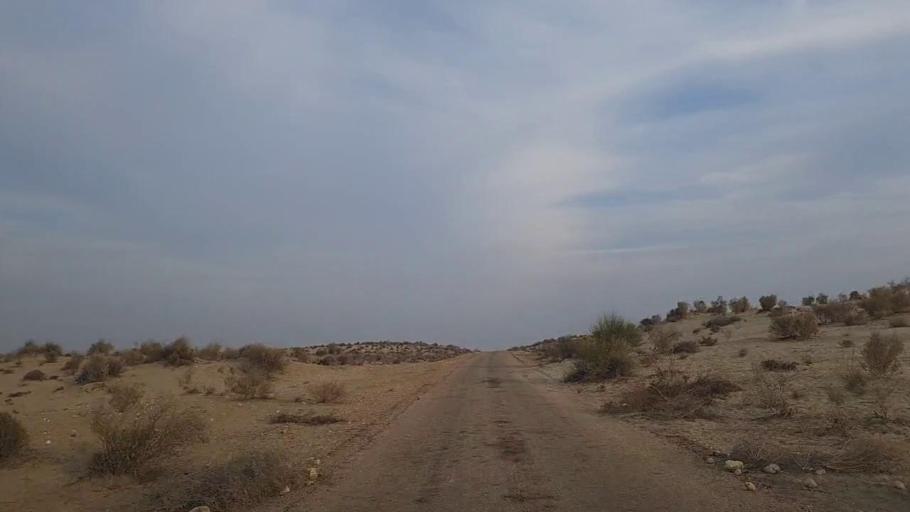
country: PK
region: Sindh
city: Jam Sahib
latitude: 26.4926
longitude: 68.5457
